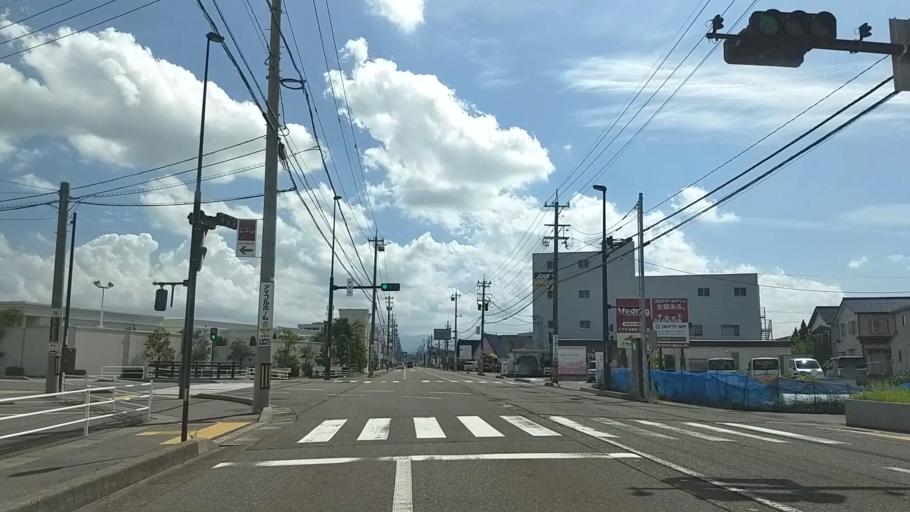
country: JP
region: Ishikawa
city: Kanazawa-shi
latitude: 36.6142
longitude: 136.6314
